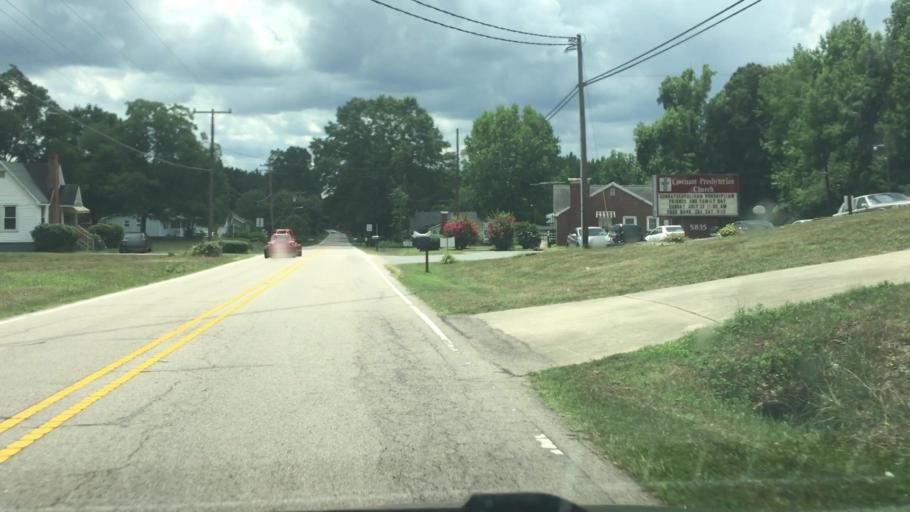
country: US
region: North Carolina
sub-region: Rowan County
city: Enochville
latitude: 35.4952
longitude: -80.6658
